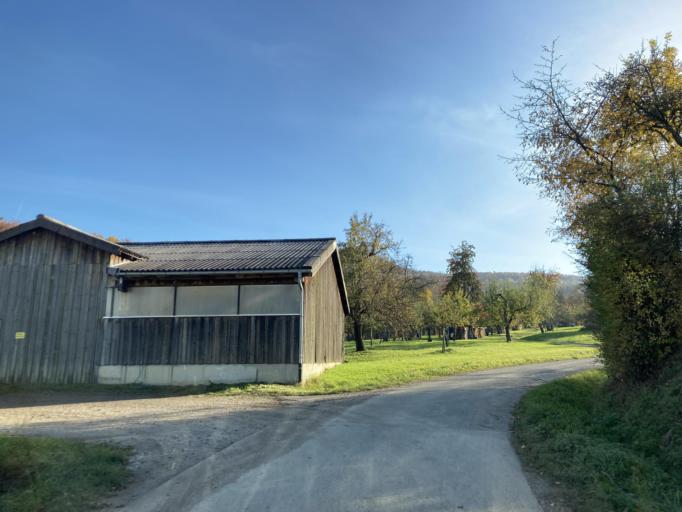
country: DE
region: Baden-Wuerttemberg
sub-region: Tuebingen Region
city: Mossingen
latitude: 48.3901
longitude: 9.0415
